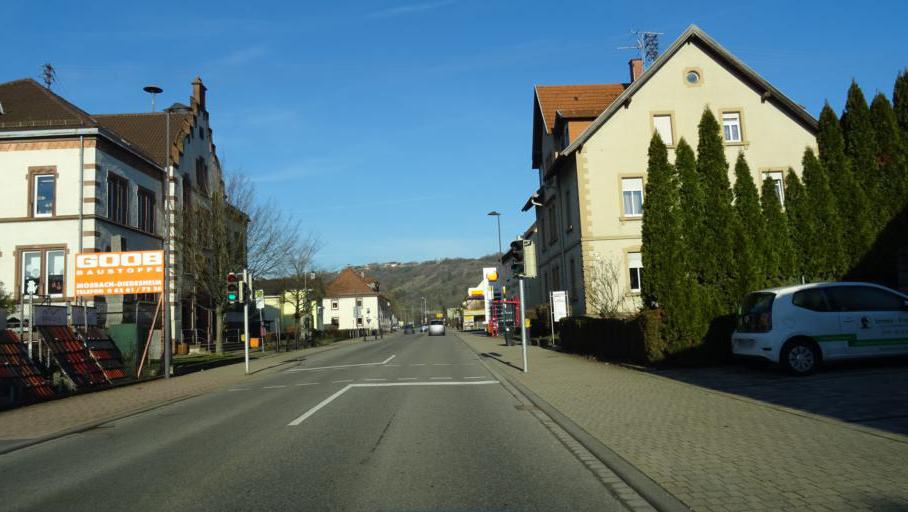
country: DE
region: Baden-Wuerttemberg
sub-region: Karlsruhe Region
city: Obrigheim
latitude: 49.3498
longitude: 9.1047
